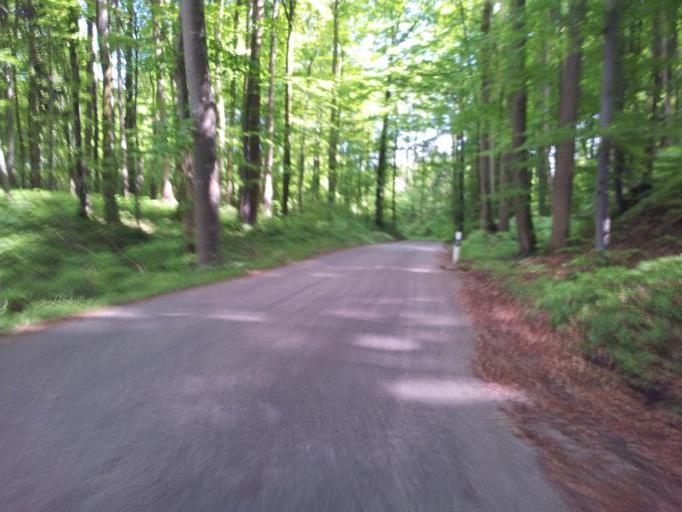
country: CH
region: Aargau
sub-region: Bezirk Bremgarten
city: Rudolfstetten
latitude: 47.3878
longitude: 8.3732
